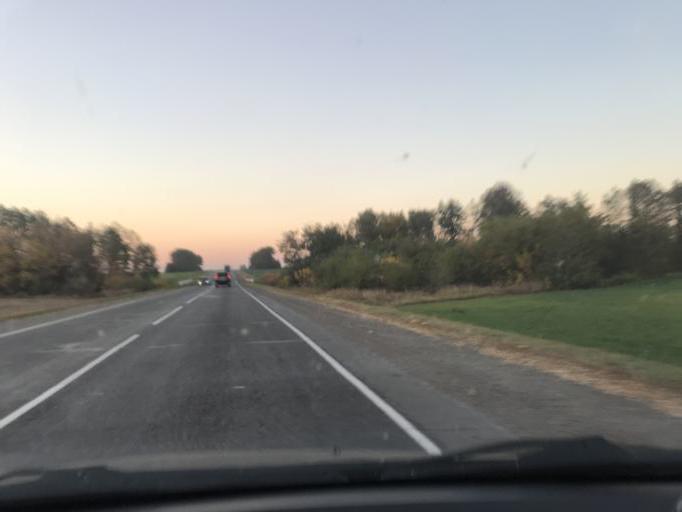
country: BY
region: Gomel
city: Horad Rechytsa
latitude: 52.2042
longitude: 30.5373
